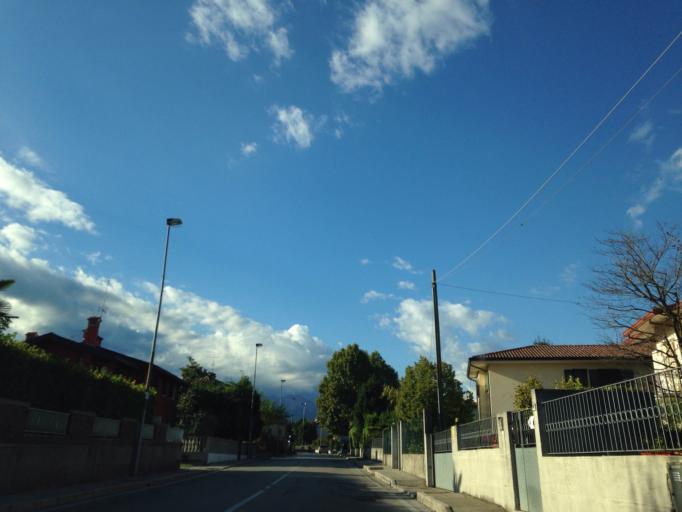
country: IT
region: Friuli Venezia Giulia
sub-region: Provincia di Pordenone
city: Pordenone
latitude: 45.9579
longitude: 12.6427
